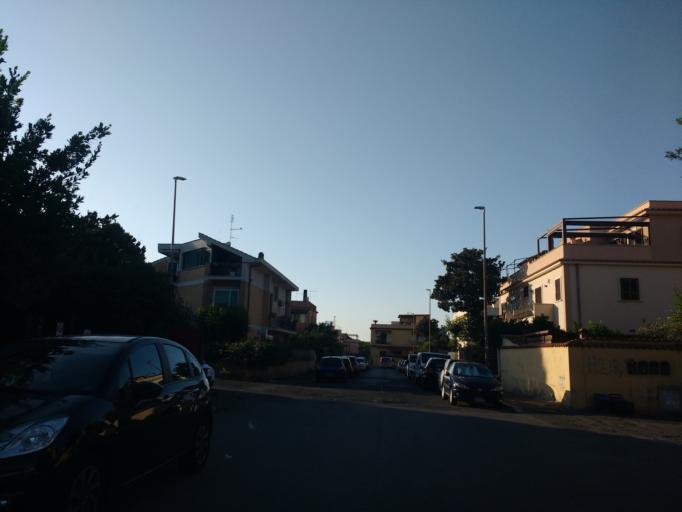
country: IT
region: Latium
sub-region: Citta metropolitana di Roma Capitale
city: Vitinia
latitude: 41.7836
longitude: 12.3690
